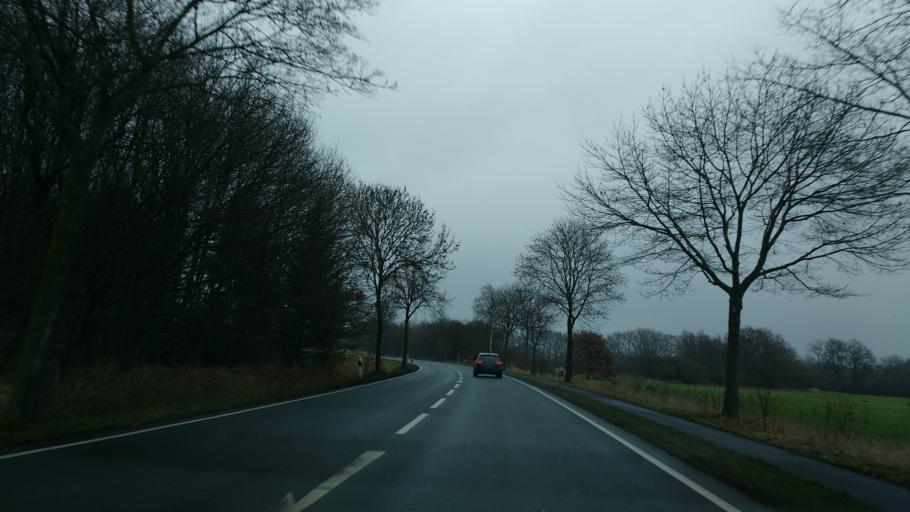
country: DE
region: Lower Saxony
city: Garbsen
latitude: 52.4322
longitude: 9.5787
